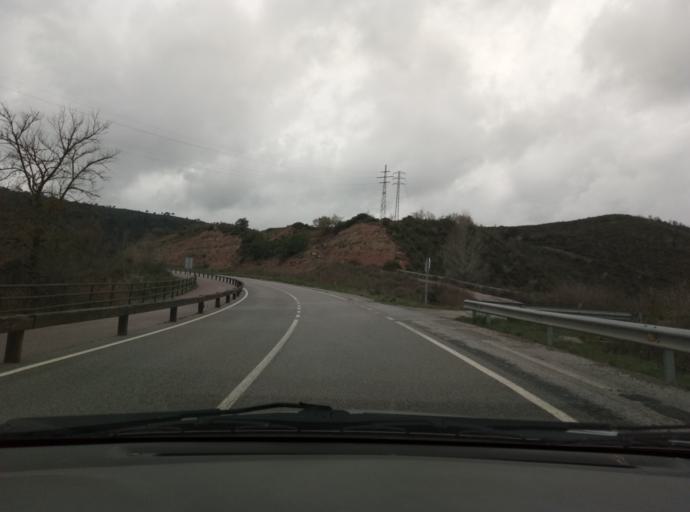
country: ES
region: Catalonia
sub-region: Provincia de Barcelona
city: Jorba
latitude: 41.6248
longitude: 1.4994
